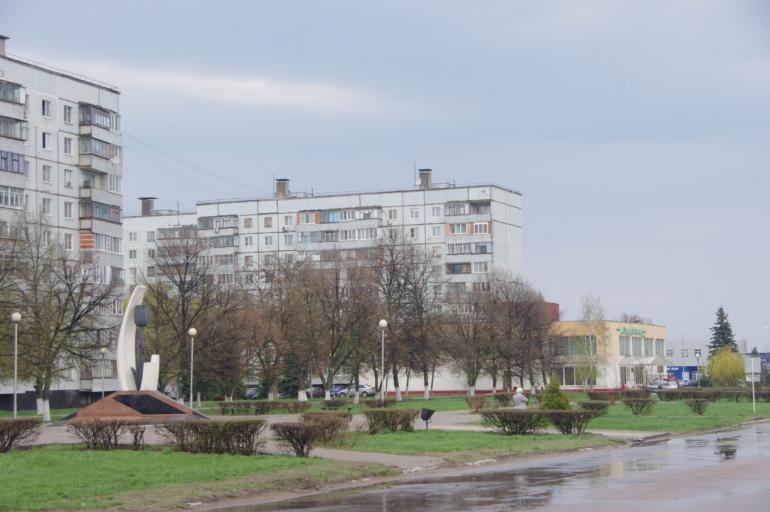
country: RU
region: Kursk
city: Kurchatov
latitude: 51.6561
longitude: 35.6744
